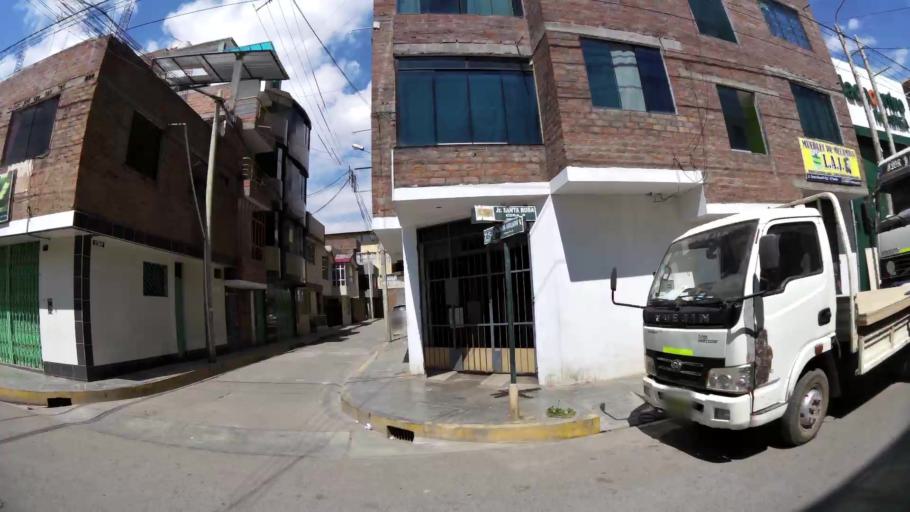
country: PE
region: Junin
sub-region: Provincia de Huancayo
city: El Tambo
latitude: -12.0669
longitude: -75.2175
